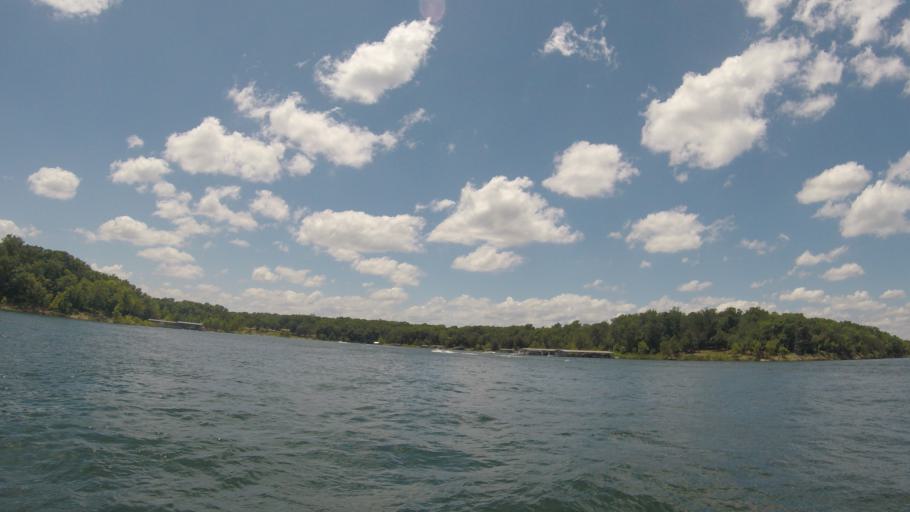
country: US
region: Missouri
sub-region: Barry County
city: Shell Knob
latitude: 36.5866
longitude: -93.5647
